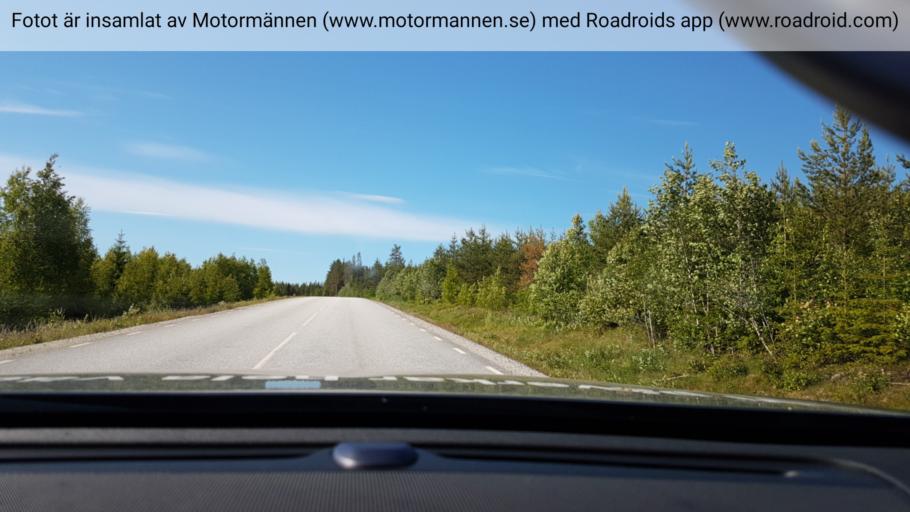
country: SE
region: Vaesterbotten
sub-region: Bjurholms Kommun
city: Bjurholm
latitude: 64.1804
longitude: 19.4016
